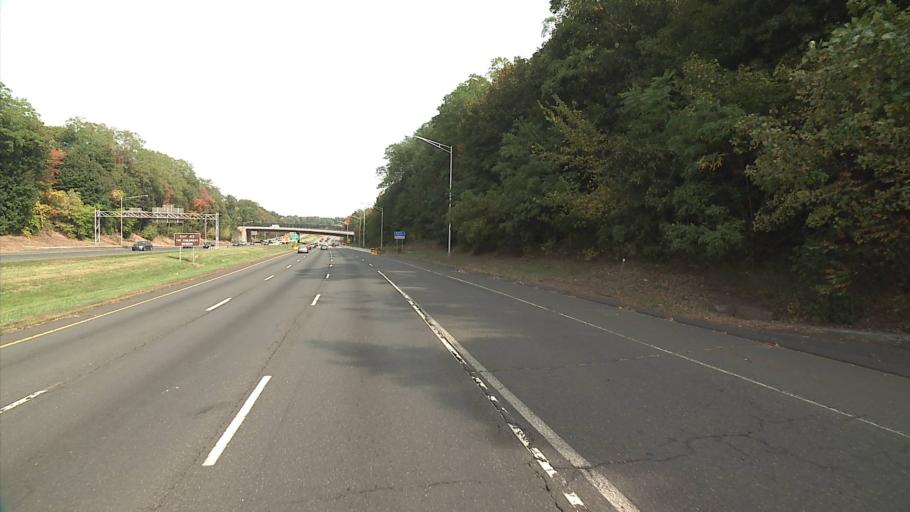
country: US
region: Connecticut
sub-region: Hartford County
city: West Hartford
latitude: 41.7364
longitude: -72.7405
